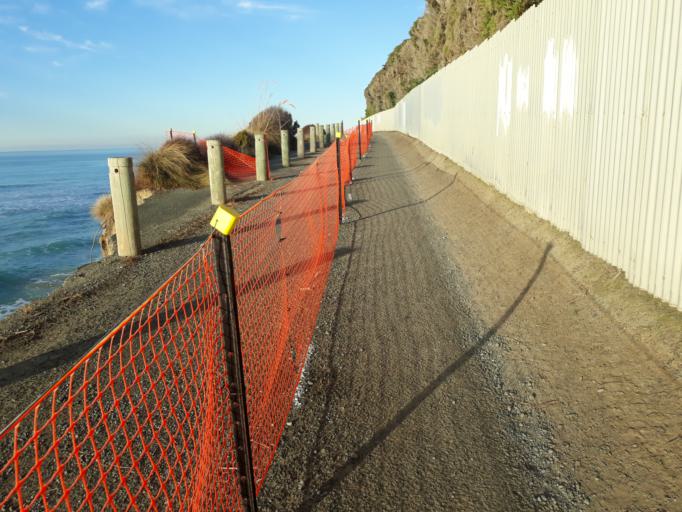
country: NZ
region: Canterbury
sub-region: Timaru District
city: Timaru
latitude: -44.4138
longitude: 171.2646
